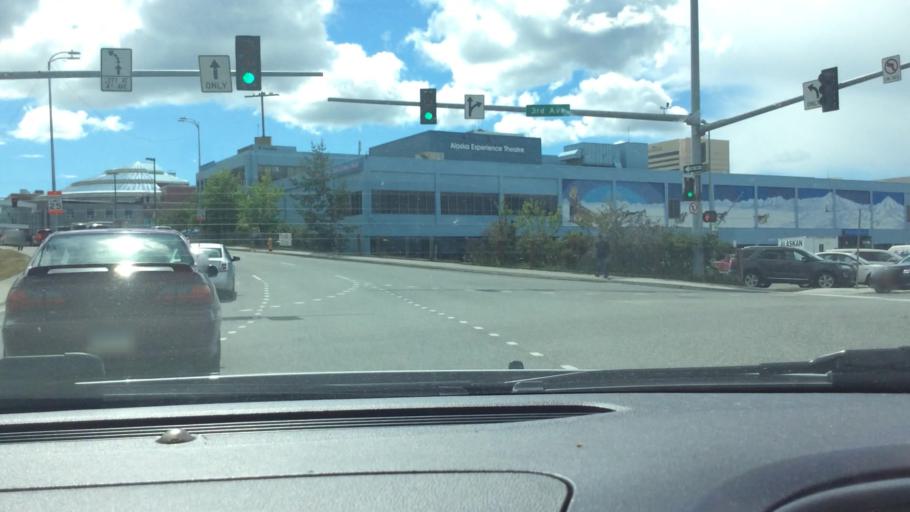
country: US
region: Alaska
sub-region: Anchorage Municipality
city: Anchorage
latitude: 61.2197
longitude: -149.8871
